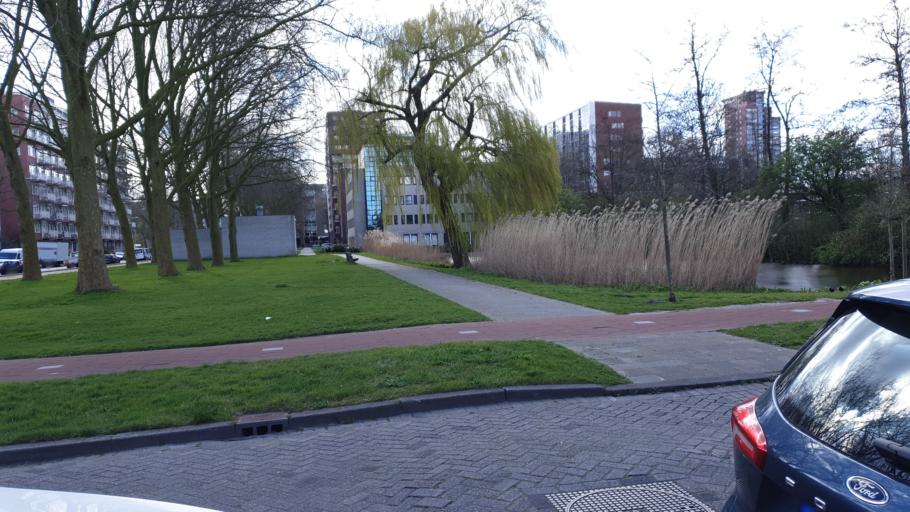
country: NL
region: South Holland
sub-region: Gemeente Rotterdam
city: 's-Gravenland
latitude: 51.9416
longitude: 4.5457
